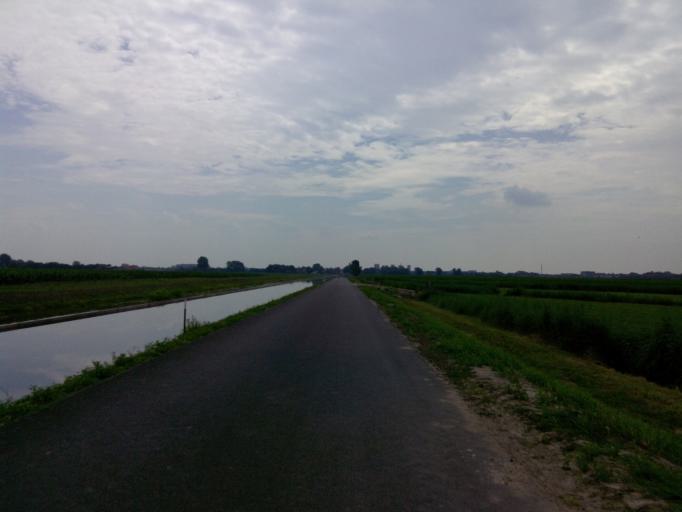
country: NL
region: Utrecht
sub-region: Gemeente Bunschoten
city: Bunschoten
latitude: 52.2169
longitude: 5.3998
